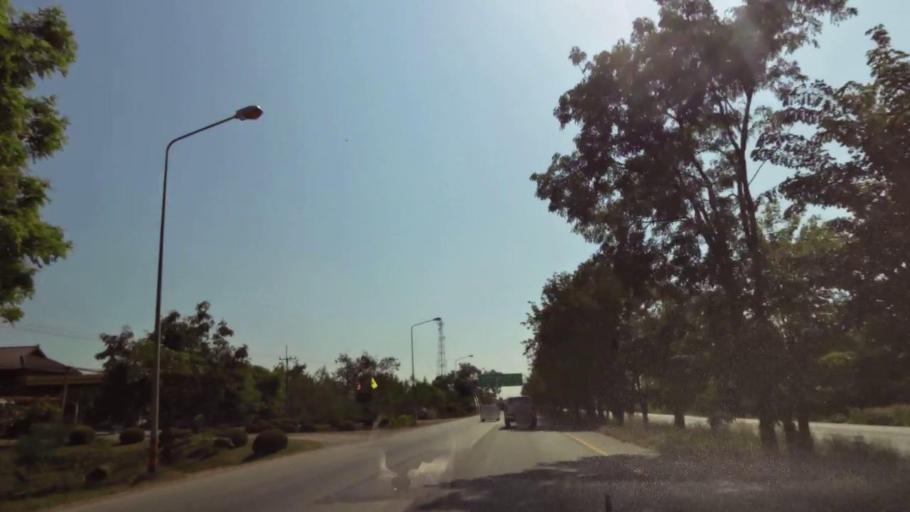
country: TH
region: Nakhon Sawan
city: Kao Liao
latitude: 15.8734
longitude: 100.1164
